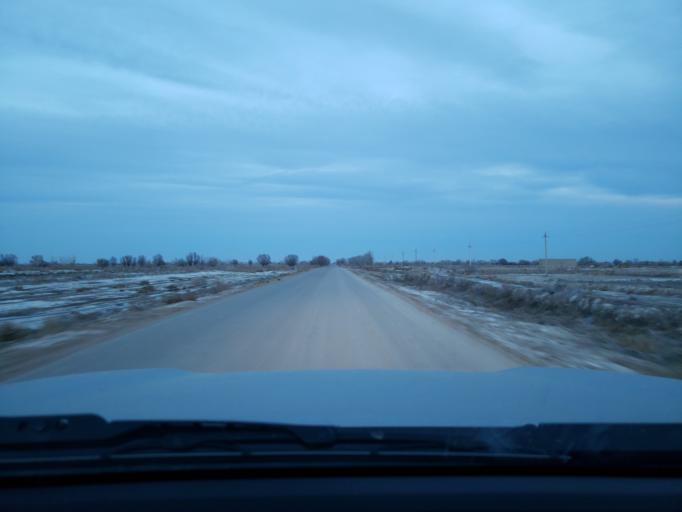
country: TM
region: Dasoguz
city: Tagta
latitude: 41.6193
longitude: 60.0541
